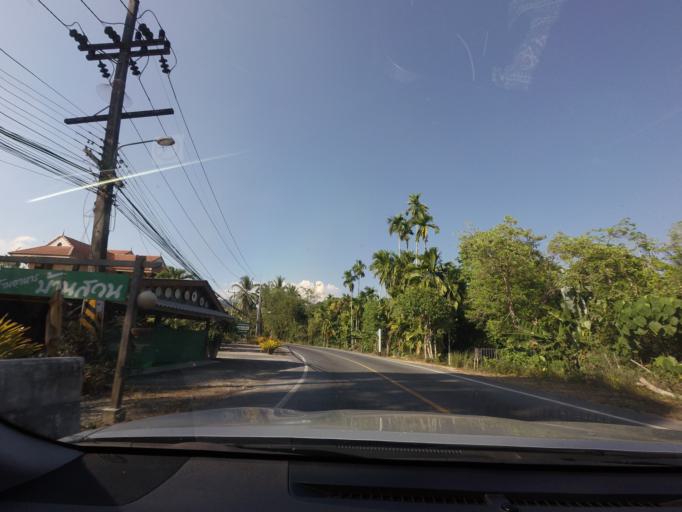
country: TH
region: Phangnga
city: Takua Thung
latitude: 8.2760
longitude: 98.3712
